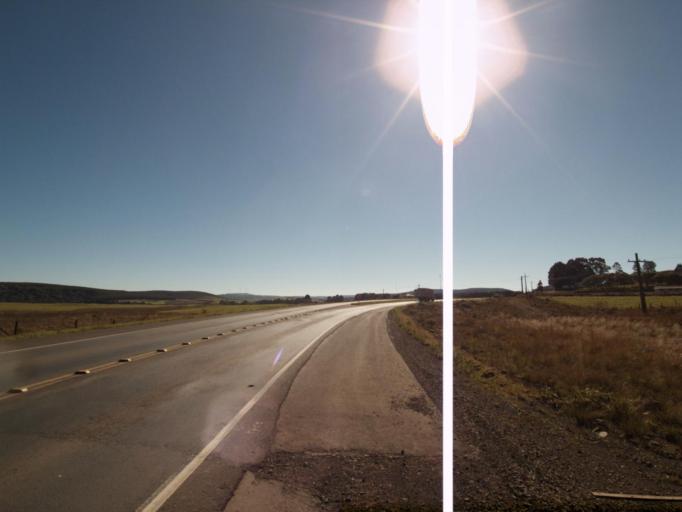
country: BR
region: Parana
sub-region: Palmas
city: Palmas
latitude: -26.6865
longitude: -51.5664
